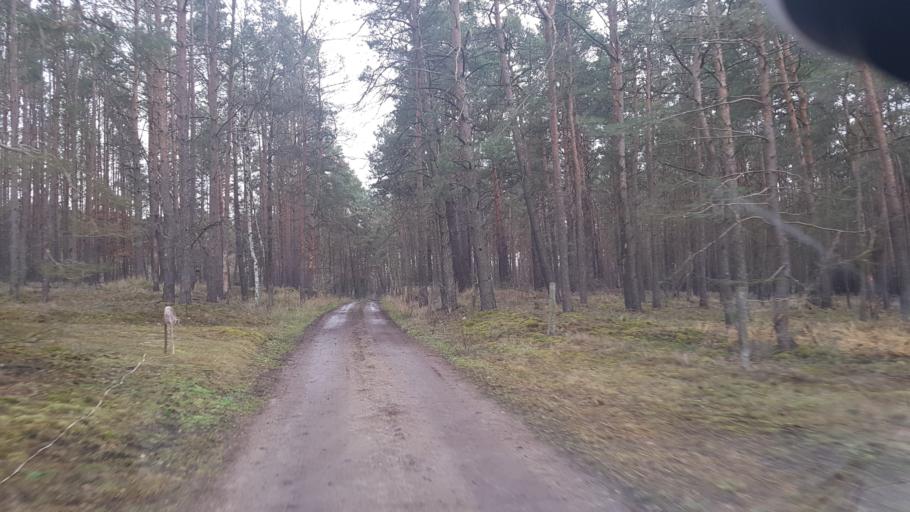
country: DE
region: Brandenburg
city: Ruckersdorf
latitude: 51.6013
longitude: 13.5933
